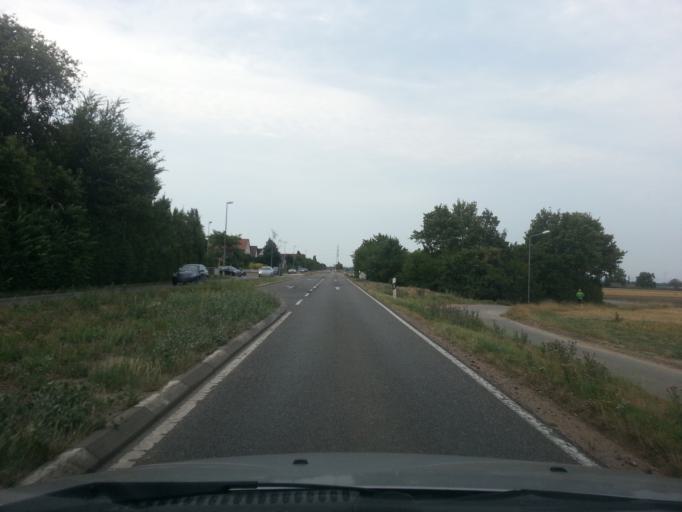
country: DE
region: Rheinland-Pfalz
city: Bobenheim-Roxheim
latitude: 49.5740
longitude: 8.3539
